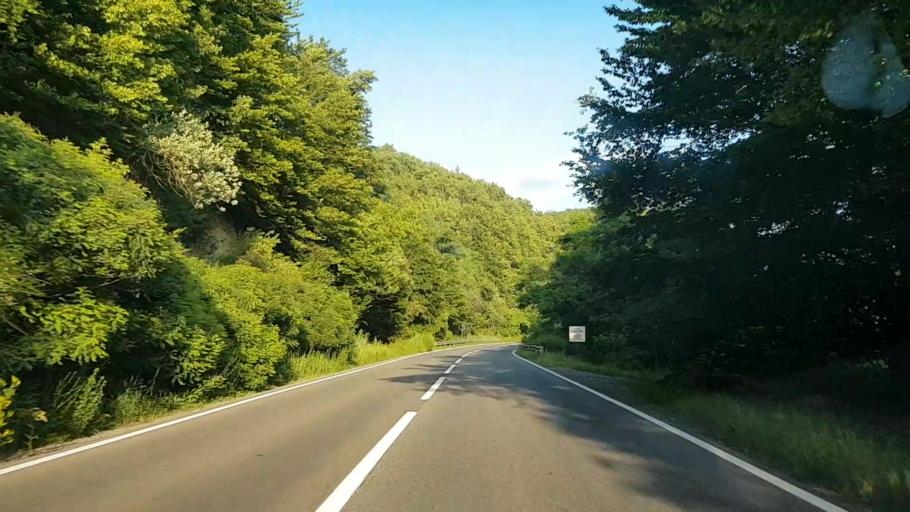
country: RO
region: Harghita
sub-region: Comuna Corund
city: Corund
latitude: 46.4489
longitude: 25.2247
